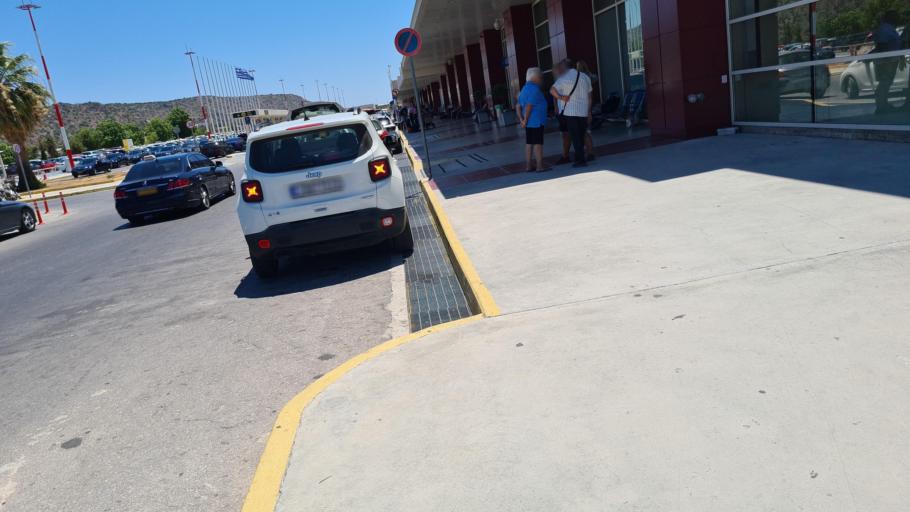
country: GR
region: Crete
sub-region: Nomos Chanias
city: Mouzouras
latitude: 35.5405
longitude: 24.1393
